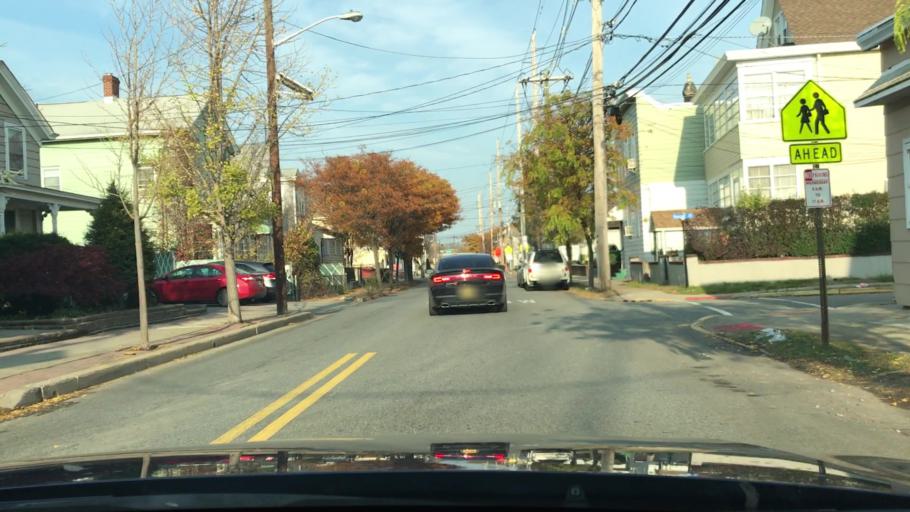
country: US
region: New Jersey
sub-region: Bergen County
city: Wallington
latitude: 40.8526
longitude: -74.1114
